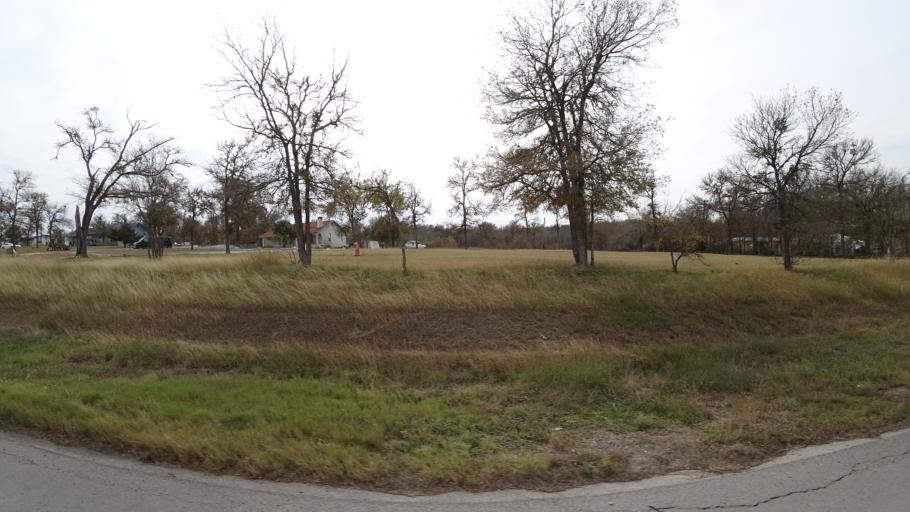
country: US
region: Texas
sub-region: Travis County
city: Garfield
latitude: 30.1494
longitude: -97.5816
